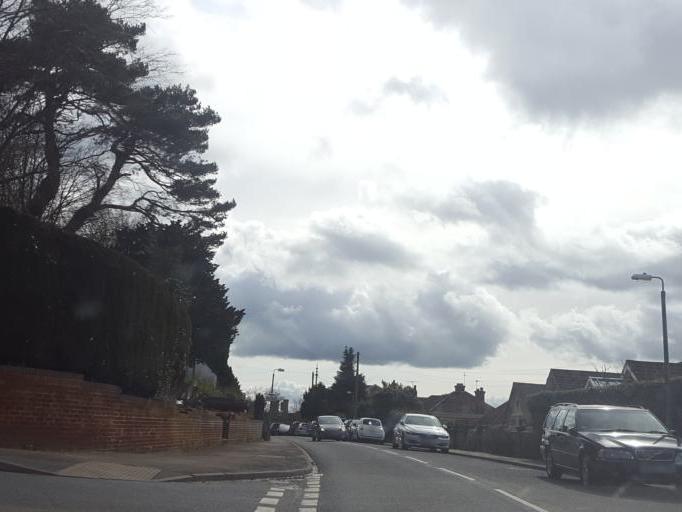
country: GB
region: England
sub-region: Worcestershire
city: Great Malvern
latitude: 52.1155
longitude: -2.3476
